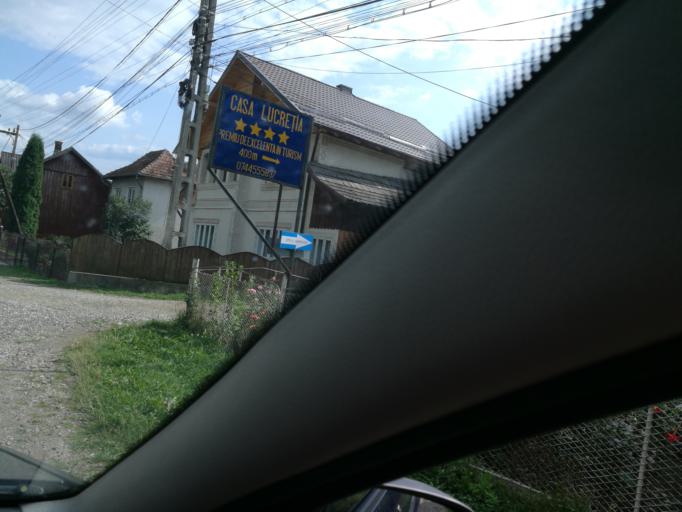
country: RO
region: Suceava
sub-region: Comuna Vama
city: Stramtura
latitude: 47.5759
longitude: 25.6869
